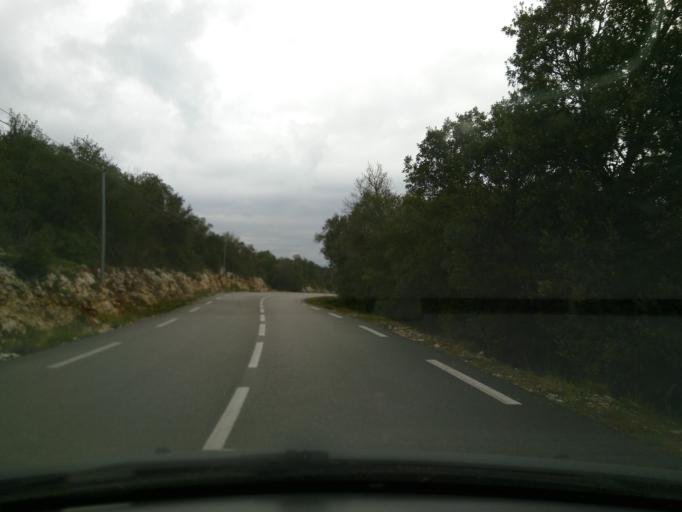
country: FR
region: Languedoc-Roussillon
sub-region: Departement du Gard
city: Barjac
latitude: 44.3341
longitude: 4.4142
